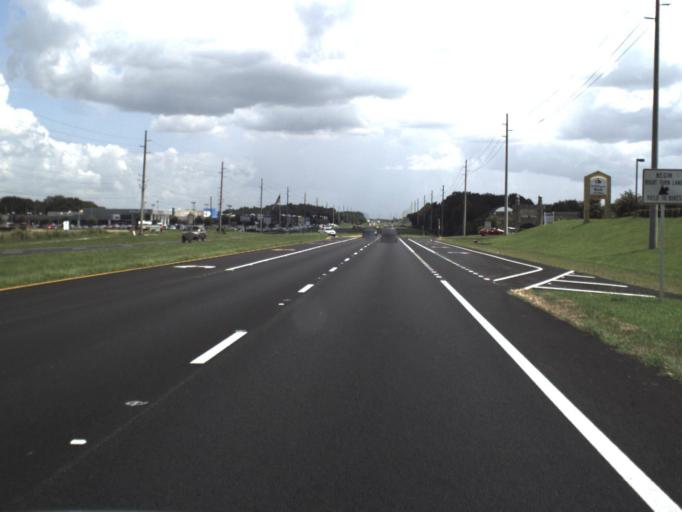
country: US
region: Florida
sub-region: Polk County
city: Cypress Gardens
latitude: 27.9842
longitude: -81.6832
